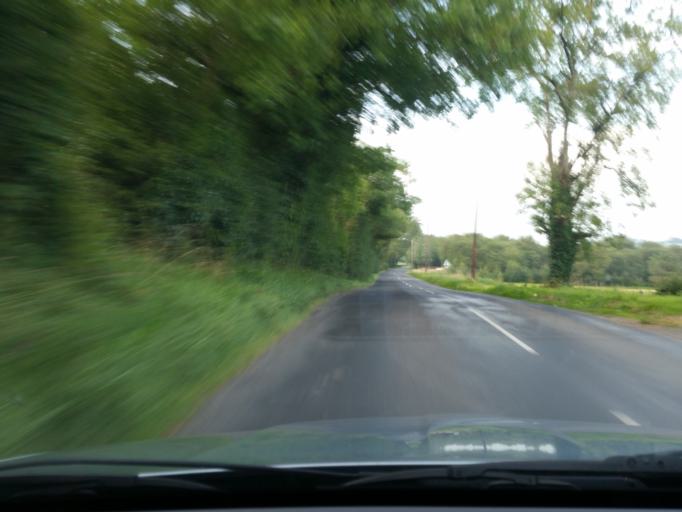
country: GB
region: Northern Ireland
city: Lisnaskea
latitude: 54.3019
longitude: -7.4158
